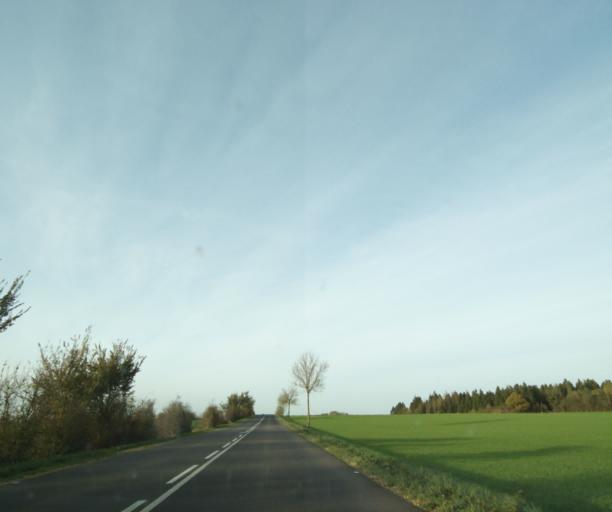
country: FR
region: Lorraine
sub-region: Departement de la Meuse
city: Etain
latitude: 49.2488
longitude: 5.6672
